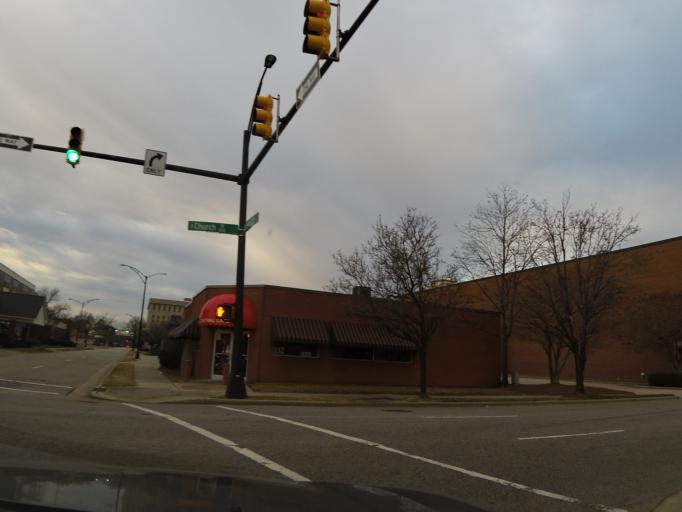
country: US
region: North Carolina
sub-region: Nash County
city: Rocky Mount
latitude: 35.9415
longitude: -77.7974
